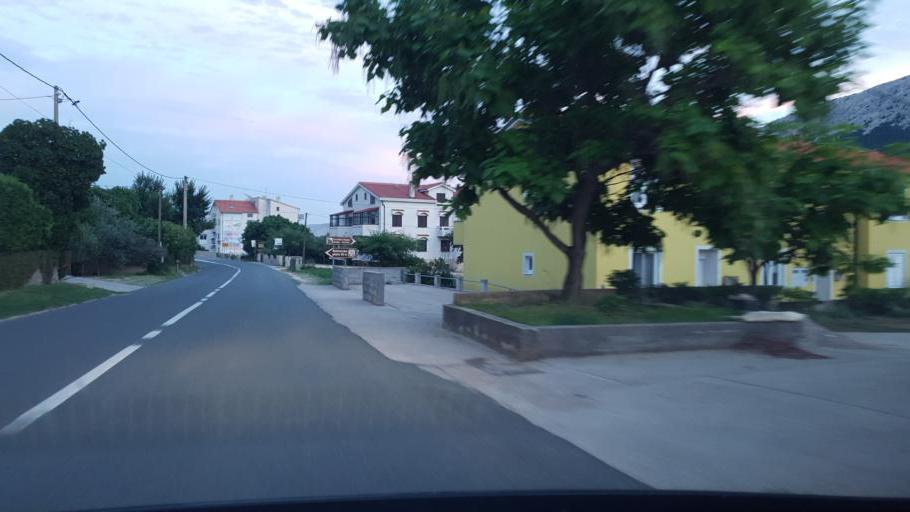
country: HR
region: Primorsko-Goranska
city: Punat
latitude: 44.9772
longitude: 14.7355
